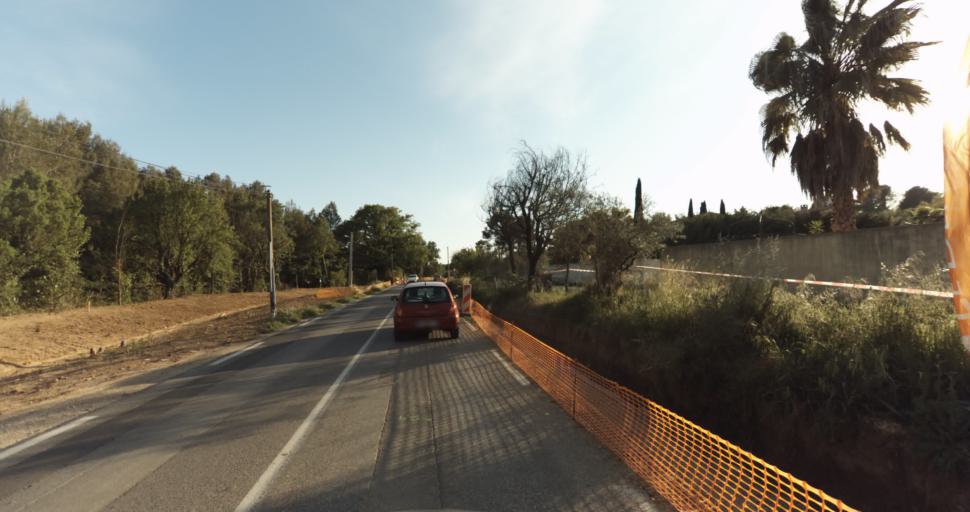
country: FR
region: Provence-Alpes-Cote d'Azur
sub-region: Departement du Var
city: La Crau
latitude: 43.1575
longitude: 6.0957
